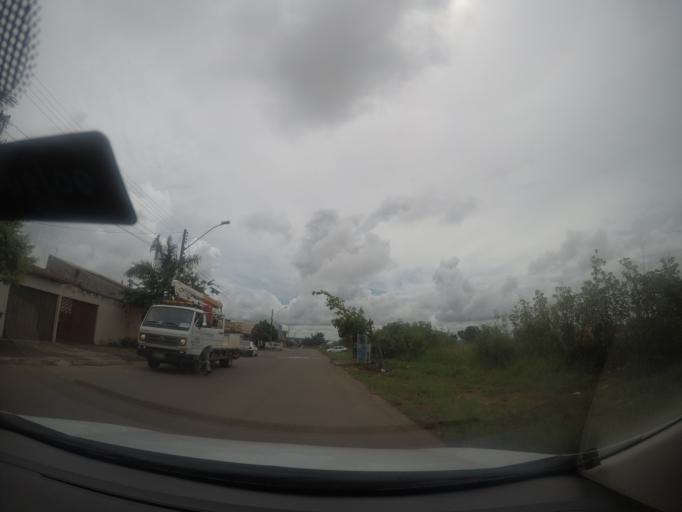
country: BR
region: Goias
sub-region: Trindade
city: Trindade
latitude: -16.6925
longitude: -49.4067
